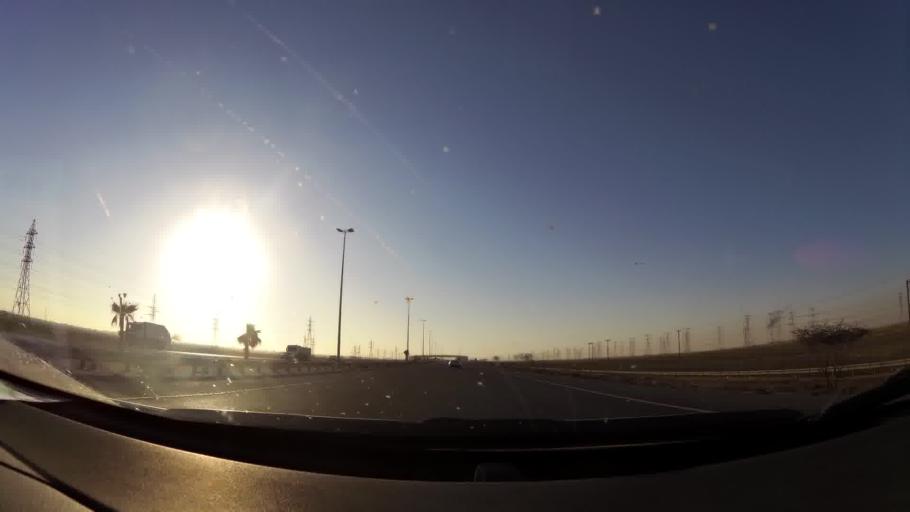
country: KW
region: Al Ahmadi
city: Al Fahahil
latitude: 28.8320
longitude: 48.2539
